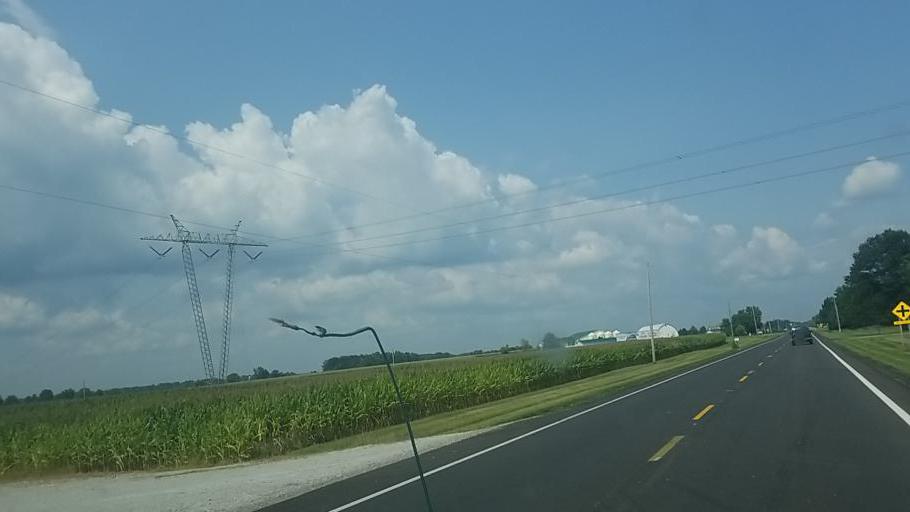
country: US
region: Ohio
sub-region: Crawford County
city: Bucyrus
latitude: 40.7737
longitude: -83.0020
